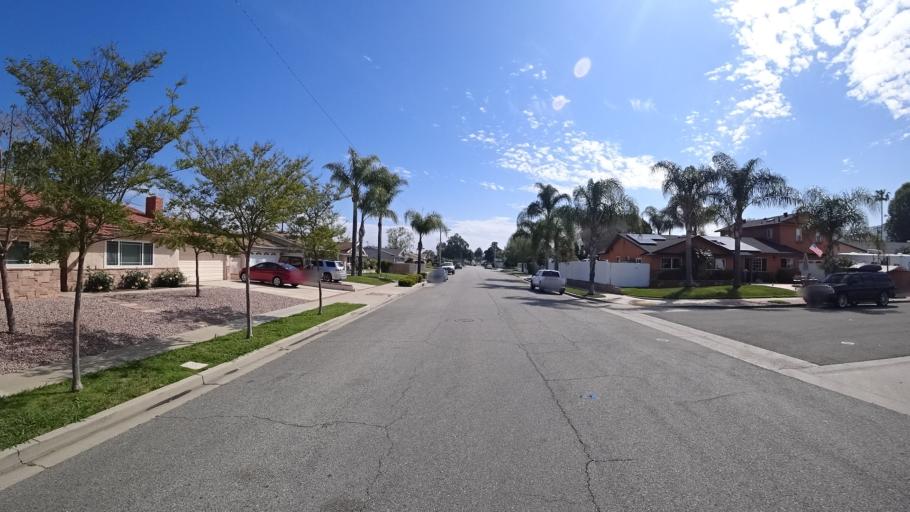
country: US
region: California
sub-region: Ventura County
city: Casa Conejo
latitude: 34.1824
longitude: -118.9432
